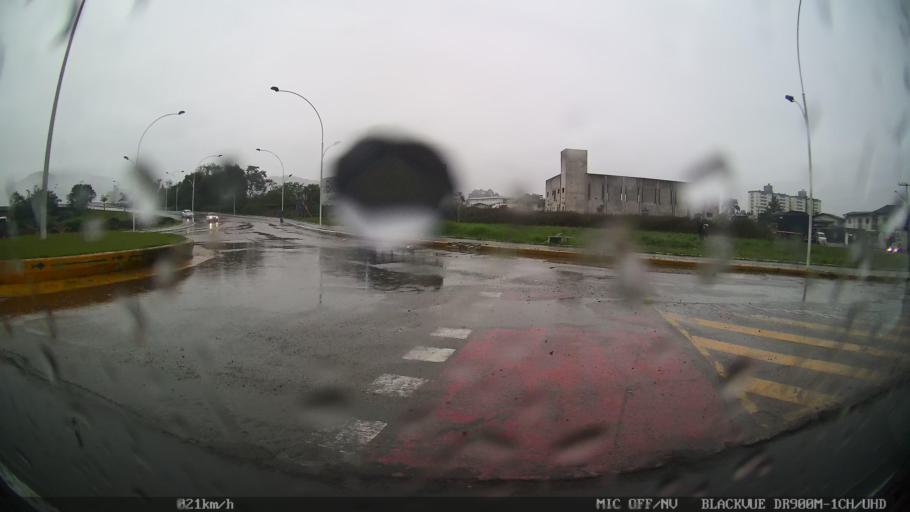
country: BR
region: Santa Catarina
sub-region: Itajai
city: Itajai
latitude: -26.9175
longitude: -48.6895
